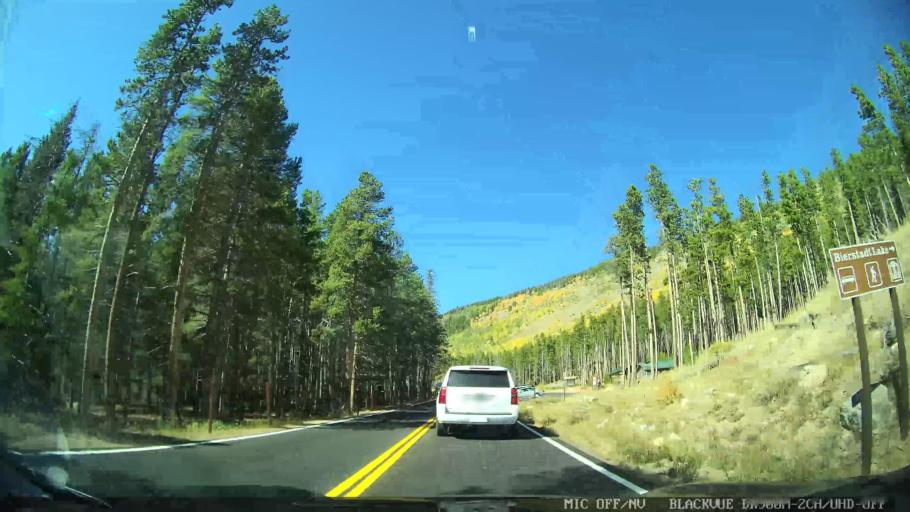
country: US
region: Colorado
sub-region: Larimer County
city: Estes Park
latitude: 40.3202
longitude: -105.6226
